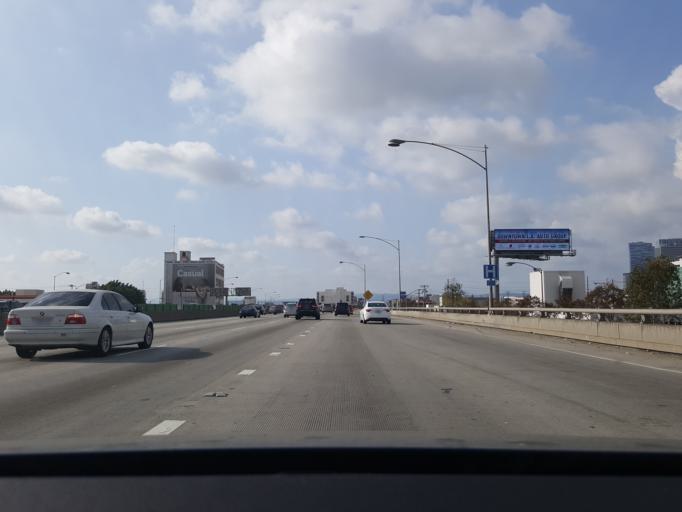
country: US
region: California
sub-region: Los Angeles County
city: Los Angeles
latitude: 34.0284
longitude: -118.2535
